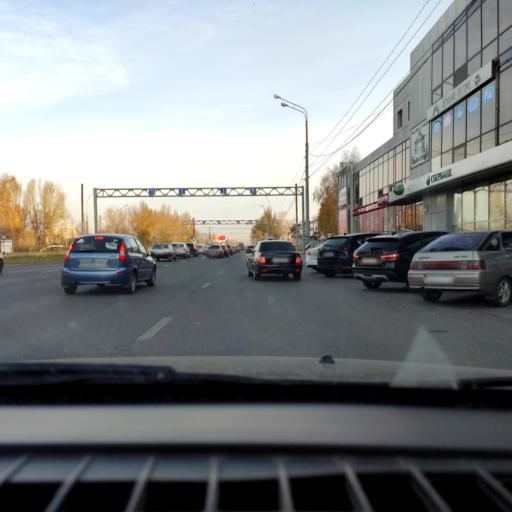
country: RU
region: Samara
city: Tol'yatti
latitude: 53.5360
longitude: 49.2836
